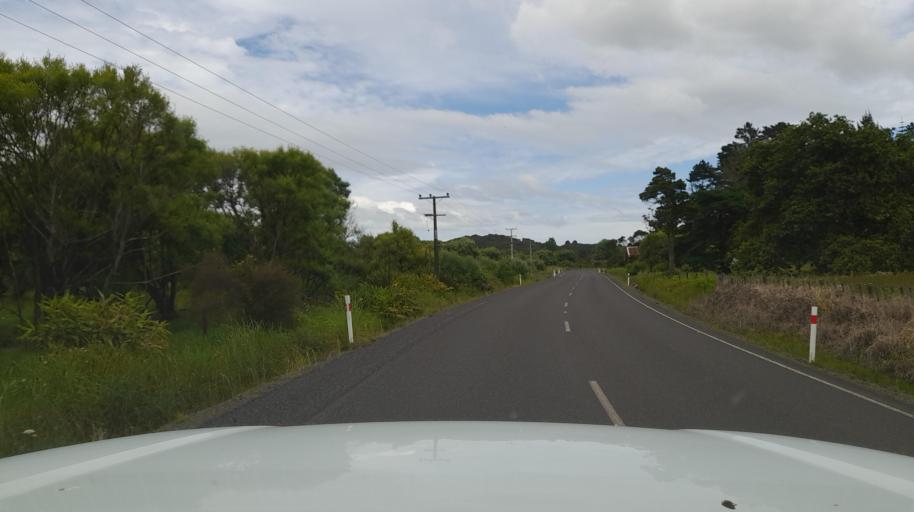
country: NZ
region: Northland
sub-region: Far North District
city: Kaitaia
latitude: -35.3861
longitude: 173.3841
